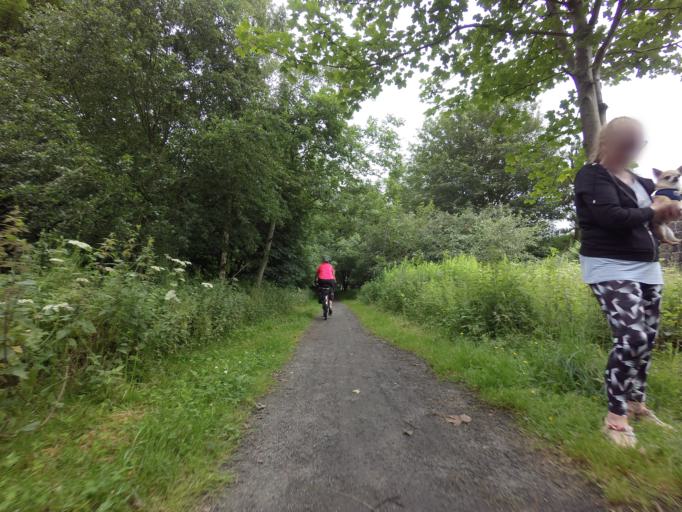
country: GB
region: Scotland
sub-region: Aberdeenshire
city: Mintlaw
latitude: 57.5195
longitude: -2.1281
